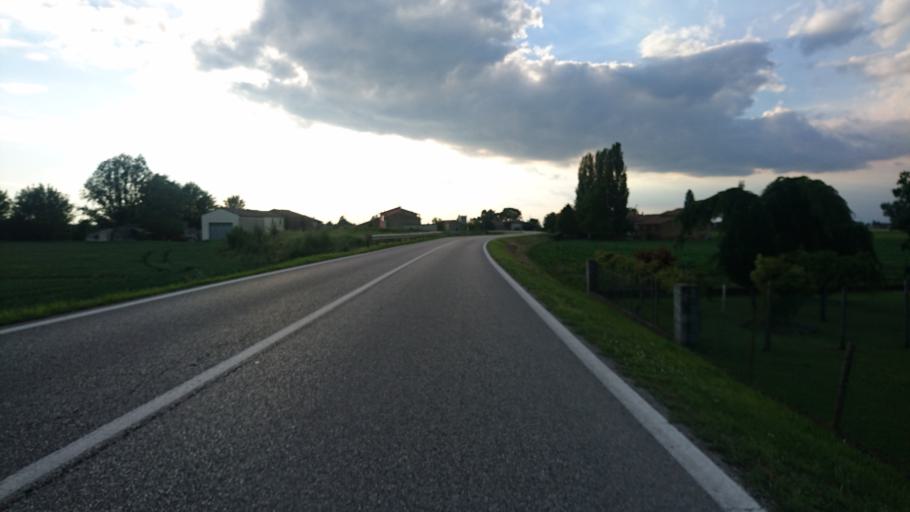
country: IT
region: Veneto
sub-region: Provincia di Rovigo
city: Ceneselli
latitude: 45.0193
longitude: 11.3598
